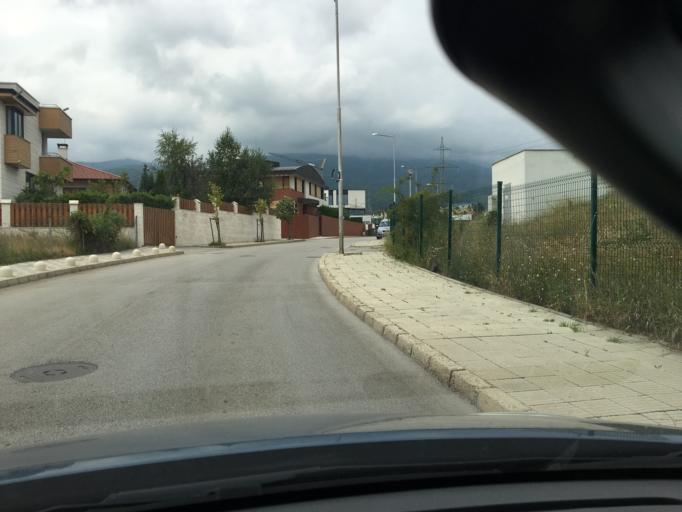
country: BG
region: Sofia-Capital
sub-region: Stolichna Obshtina
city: Sofia
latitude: 42.6170
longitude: 23.3666
